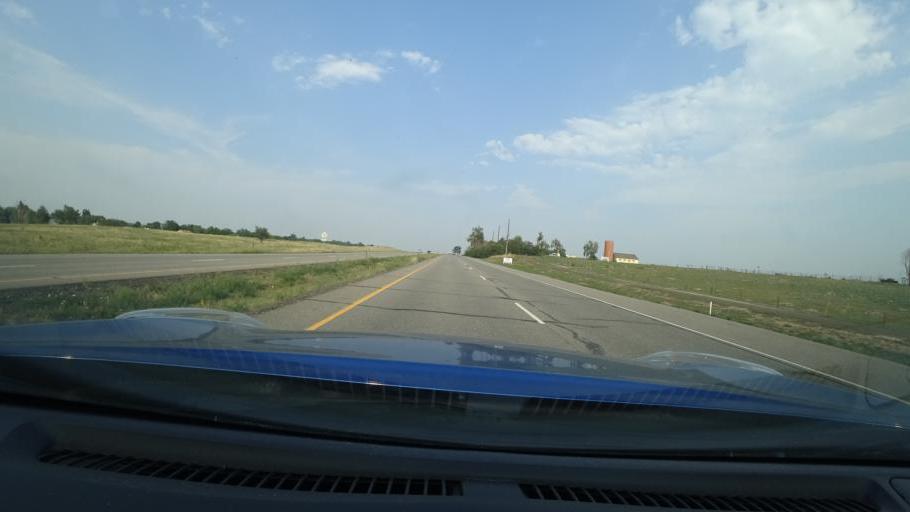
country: US
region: Colorado
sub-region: Adams County
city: Aurora
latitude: 39.7404
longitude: -104.7598
